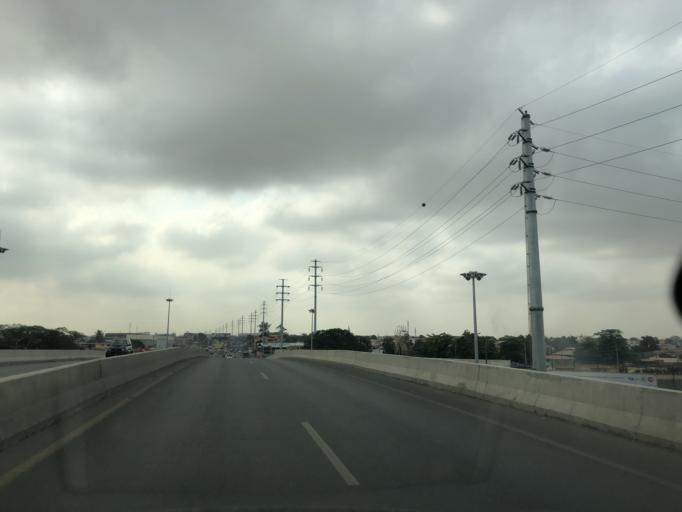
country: AO
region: Luanda
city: Luanda
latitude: -8.8344
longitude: 13.2556
